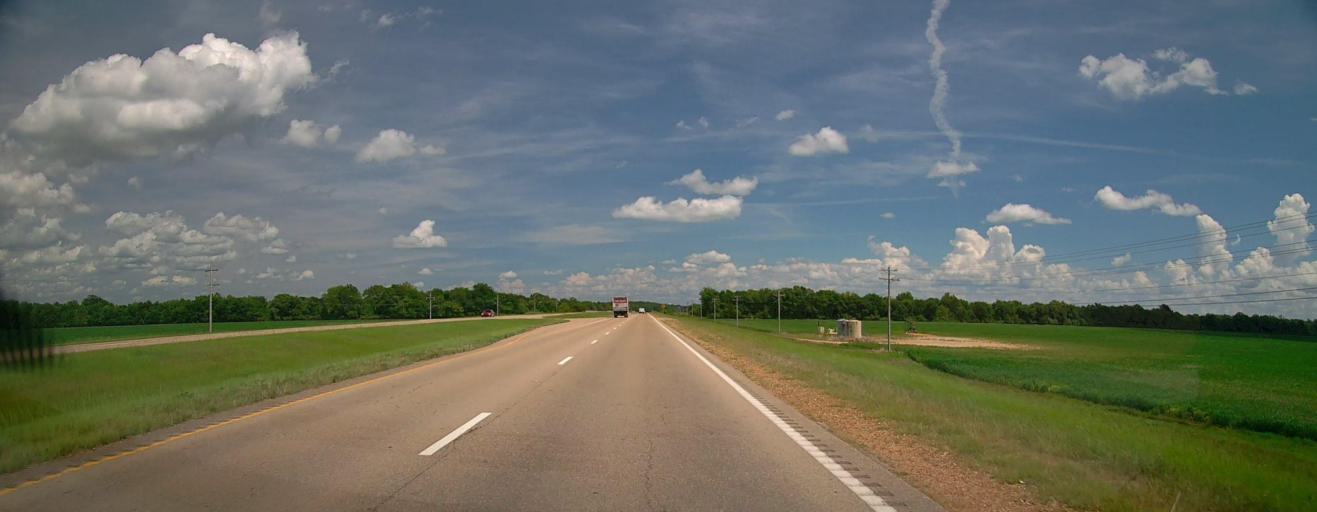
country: US
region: Mississippi
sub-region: Lee County
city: Nettleton
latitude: 34.1018
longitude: -88.6591
